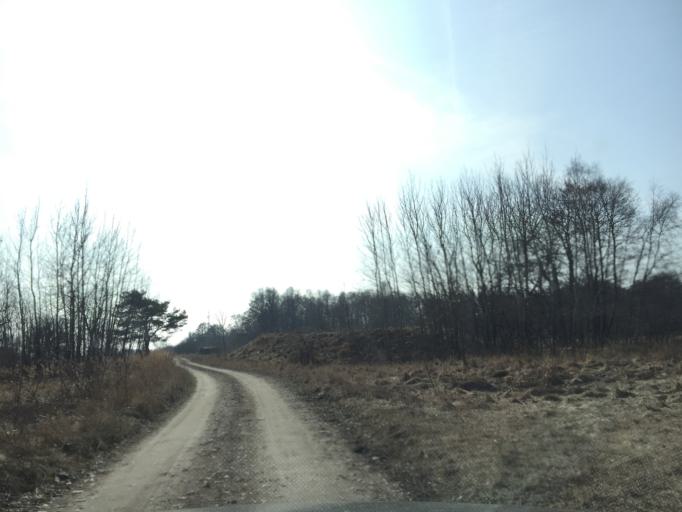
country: LV
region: Dundaga
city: Dundaga
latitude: 57.9236
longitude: 22.0610
